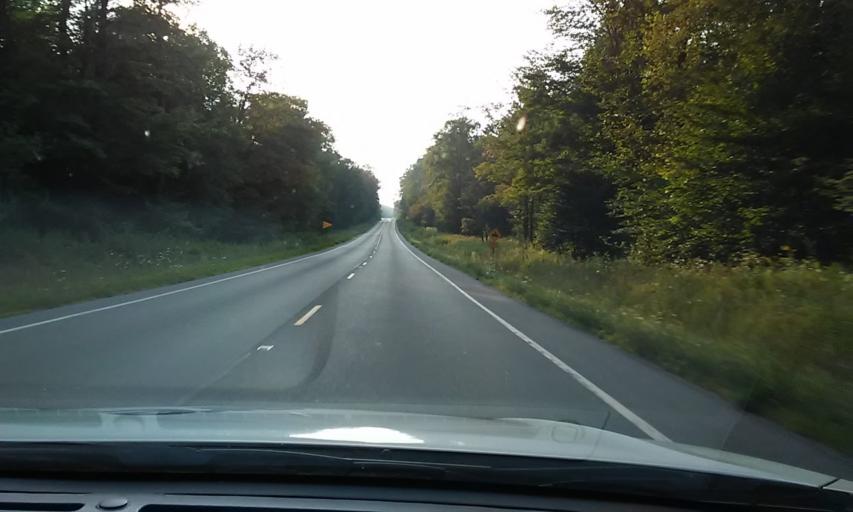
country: US
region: Pennsylvania
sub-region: McKean County
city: Kane
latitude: 41.5764
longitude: -78.9222
